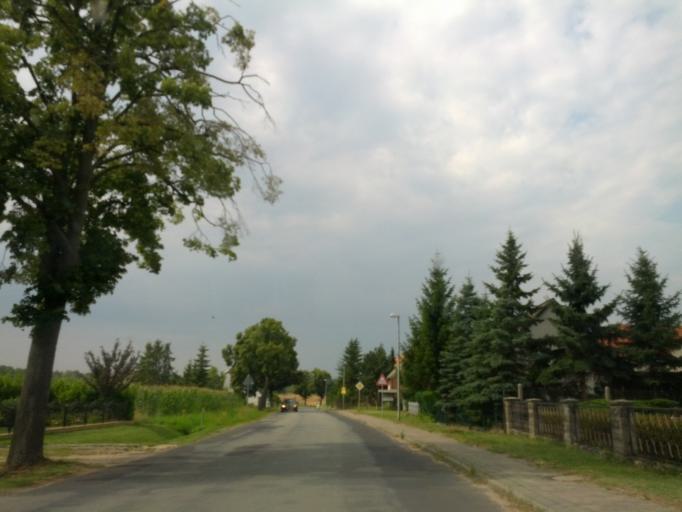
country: DE
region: Brandenburg
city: Fehrbellin
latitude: 52.7961
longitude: 12.8045
